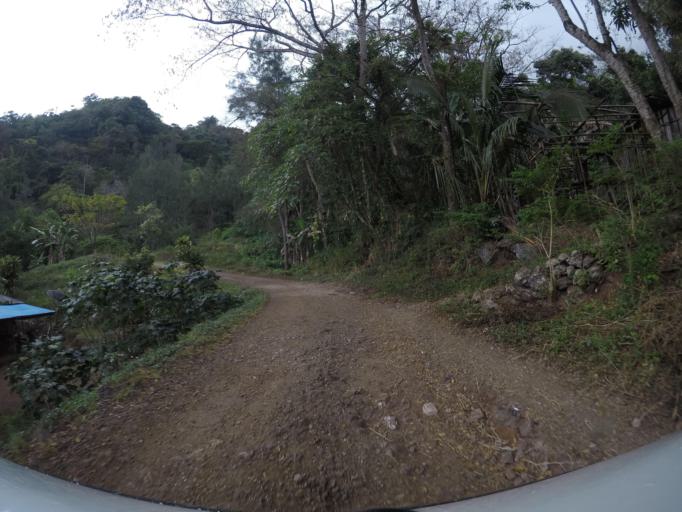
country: TL
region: Baucau
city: Baucau
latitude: -8.6463
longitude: 126.6272
